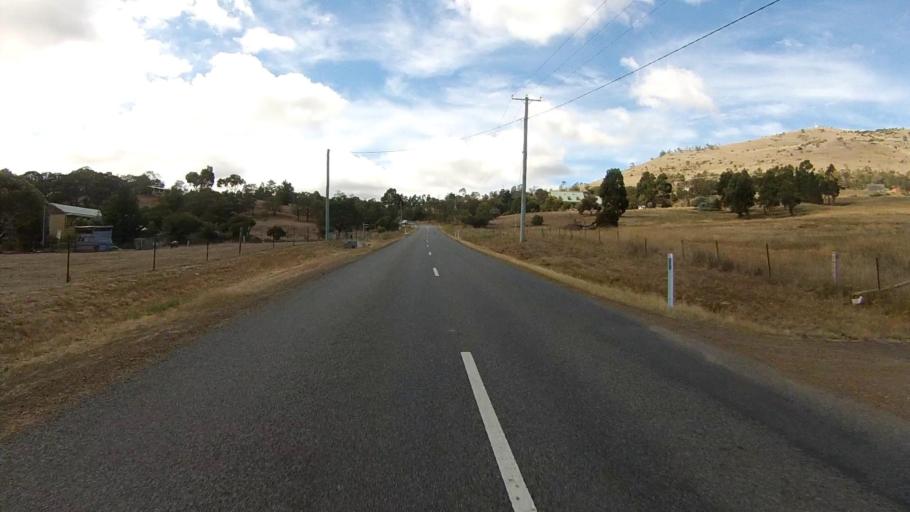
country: AU
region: Tasmania
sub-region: Glenorchy
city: Austins Ferry
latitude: -42.7248
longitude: 147.2837
